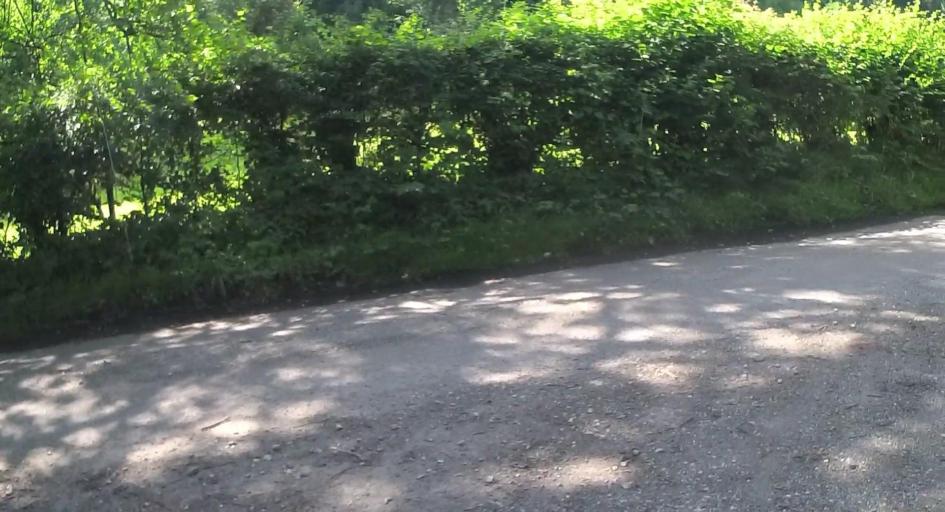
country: GB
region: England
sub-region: Hampshire
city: Kingsley
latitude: 51.1506
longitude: -0.8938
